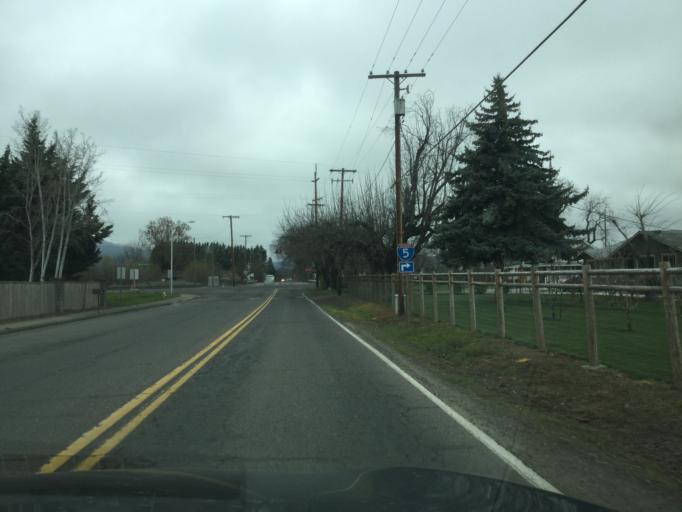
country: US
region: Oregon
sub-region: Jackson County
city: Central Point
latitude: 42.3894
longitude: -122.9316
